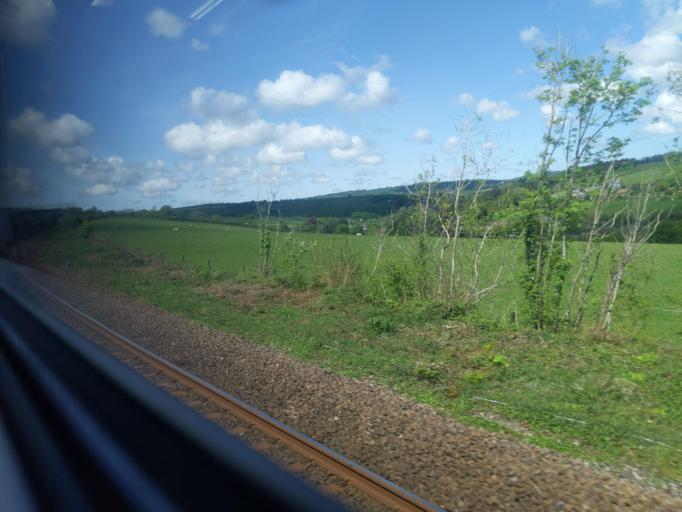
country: GB
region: England
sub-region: Cornwall
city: Liskeard
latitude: 50.4493
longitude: -4.4885
